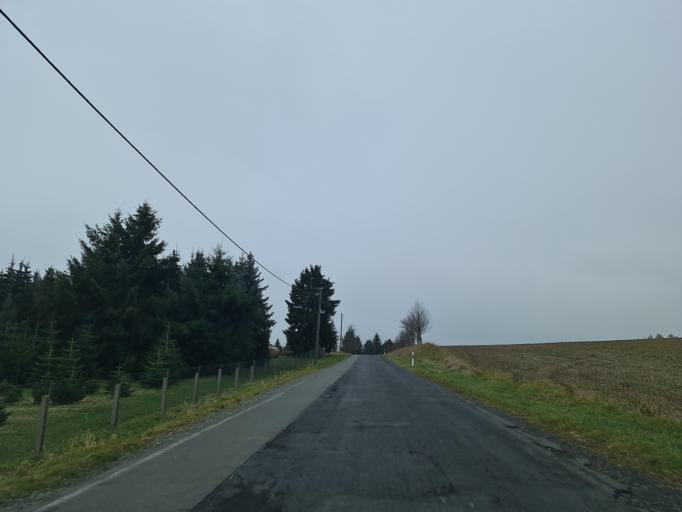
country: DE
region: Saxony
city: Mehltheuer
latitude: 50.5130
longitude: 12.0484
